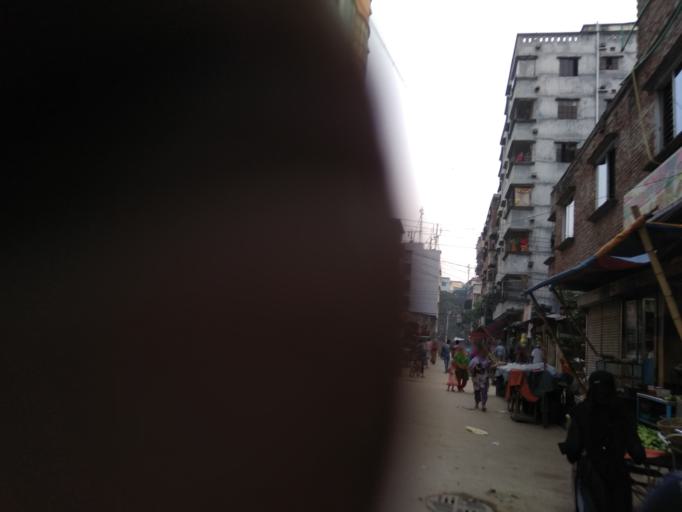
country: BD
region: Dhaka
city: Tungi
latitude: 23.8167
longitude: 90.3641
